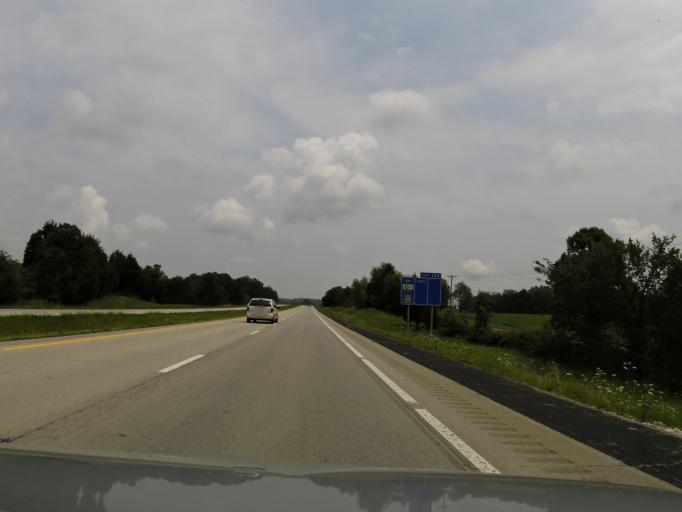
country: US
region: Kentucky
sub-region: Hardin County
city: Elizabethtown
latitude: 37.5666
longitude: -86.0487
